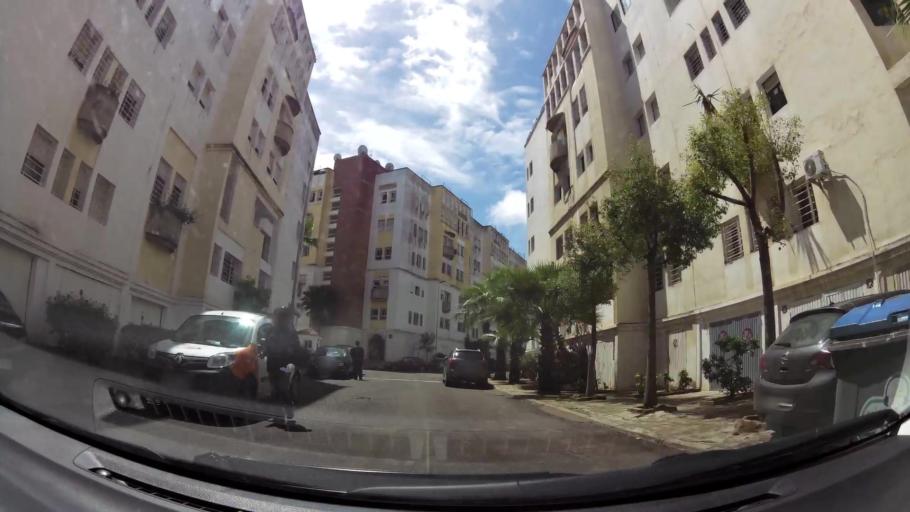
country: MA
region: Grand Casablanca
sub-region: Casablanca
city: Casablanca
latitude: 33.5587
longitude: -7.6739
